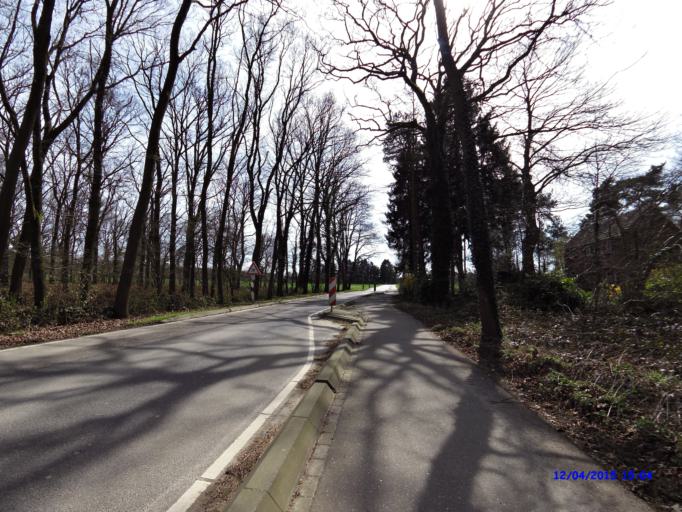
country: DE
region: North Rhine-Westphalia
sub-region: Regierungsbezirk Koln
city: Gangelt
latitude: 50.9728
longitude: 6.0220
